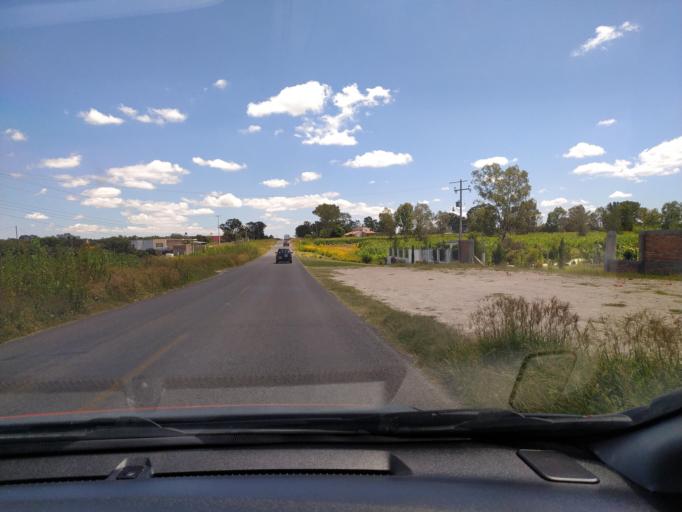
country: MX
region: Jalisco
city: San Diego de Alejandria
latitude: 21.0061
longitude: -102.0516
